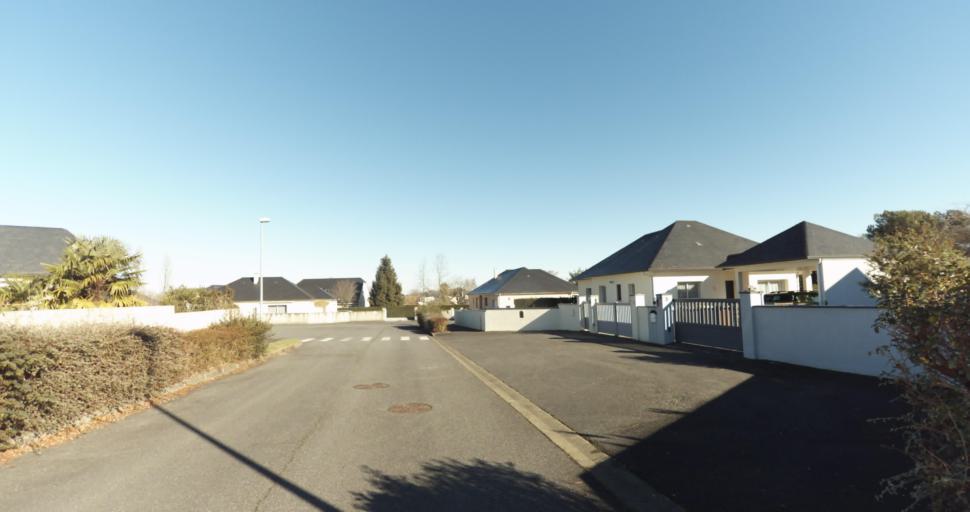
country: FR
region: Aquitaine
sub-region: Departement des Pyrenees-Atlantiques
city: Morlaas
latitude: 43.3458
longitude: -0.2690
